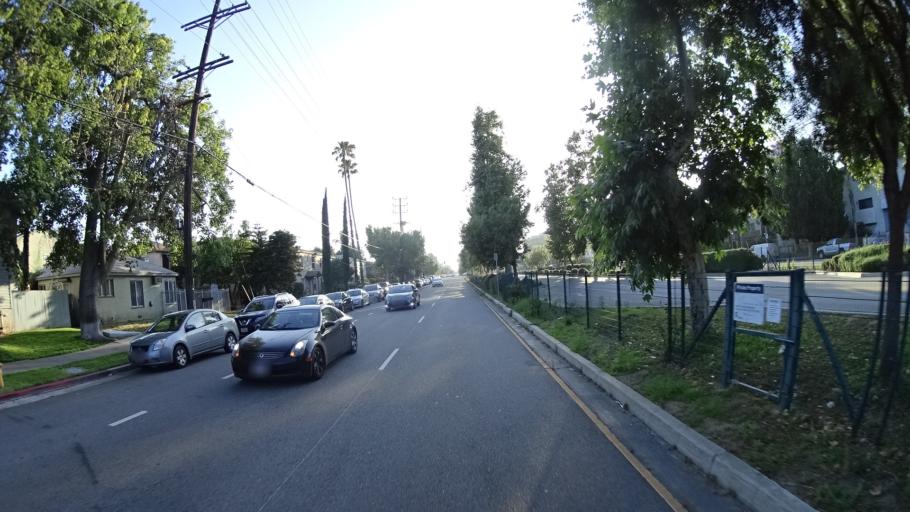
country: US
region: California
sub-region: Los Angeles County
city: North Hollywood
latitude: 34.1684
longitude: -118.3859
